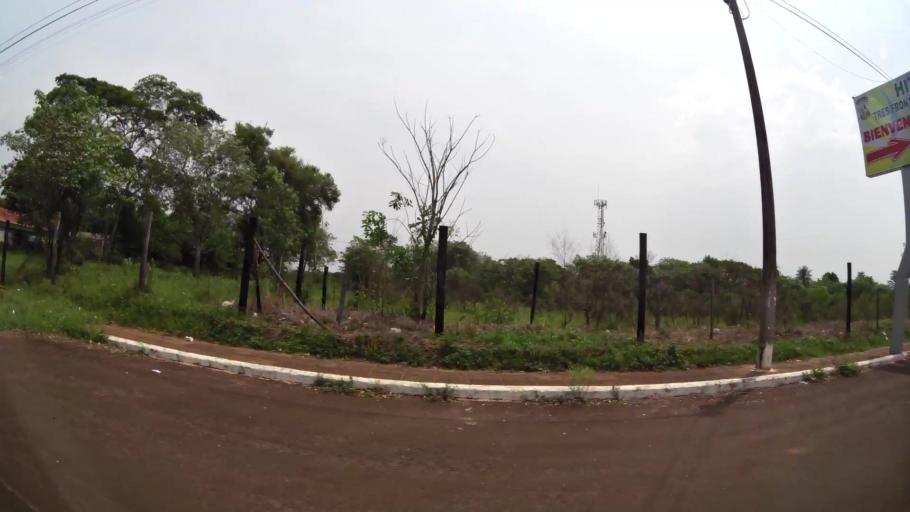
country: AR
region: Misiones
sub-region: Departamento de Iguazu
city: Puerto Iguazu
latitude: -25.5931
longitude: -54.6013
